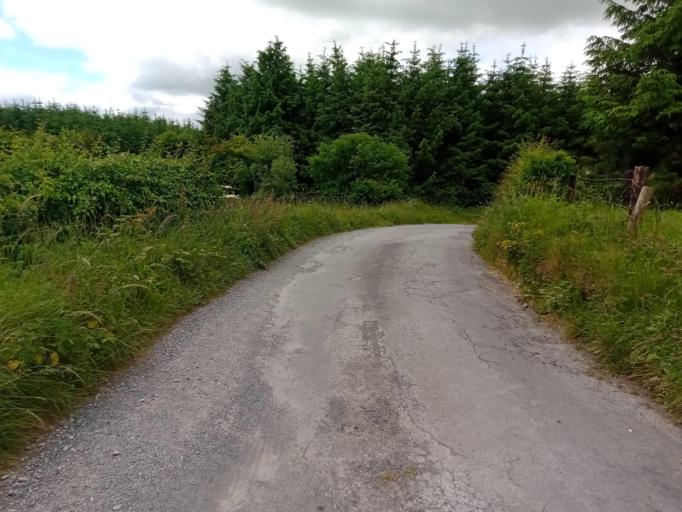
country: IE
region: Leinster
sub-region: Laois
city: Rathdowney
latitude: 52.7927
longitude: -7.4779
